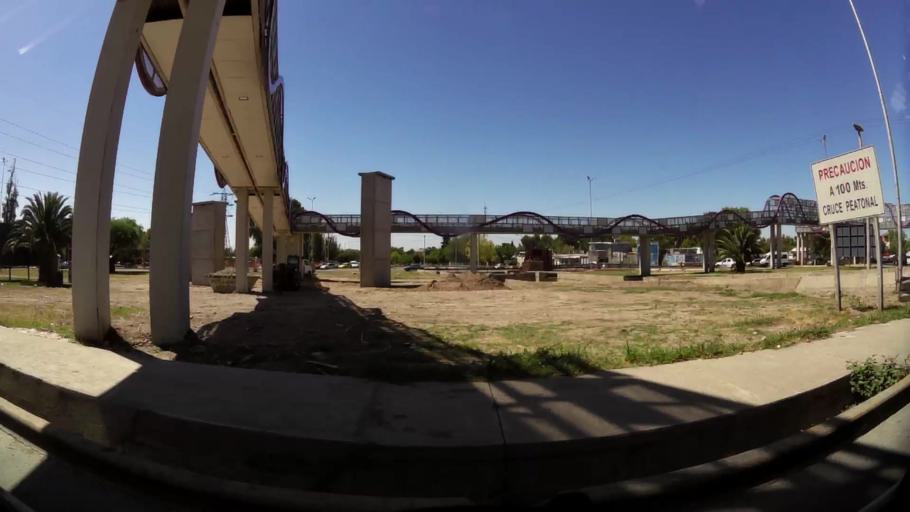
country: AR
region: Mendoza
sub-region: Departamento de Godoy Cruz
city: Godoy Cruz
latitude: -32.9242
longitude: -68.8645
